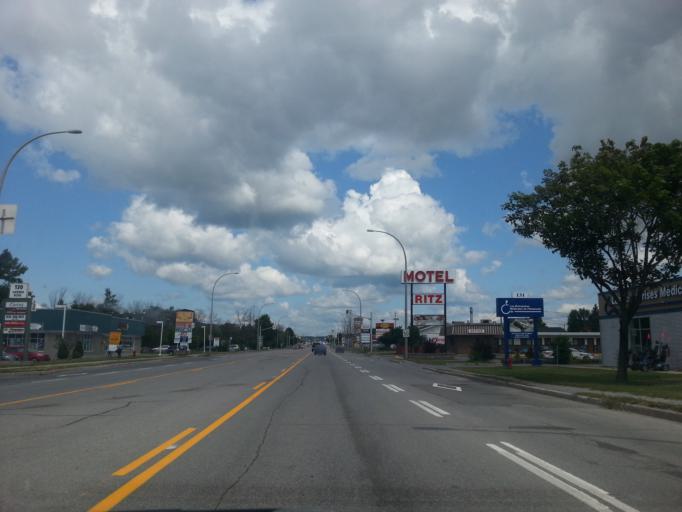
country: CA
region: Quebec
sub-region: Outaouais
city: Gatineau
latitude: 45.4676
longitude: -75.7005
